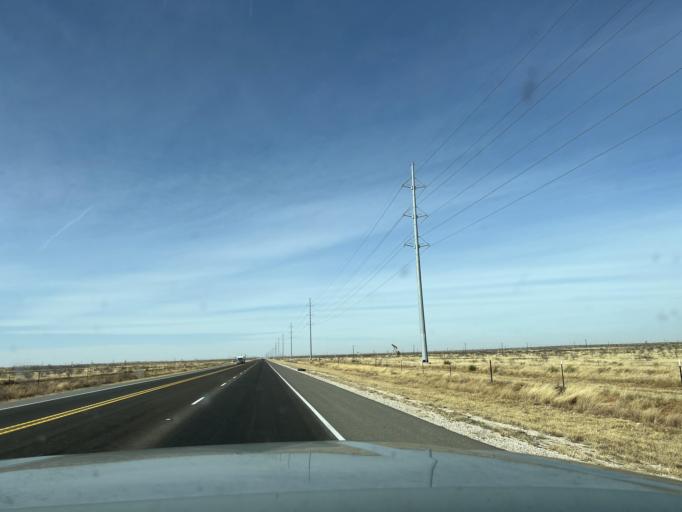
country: US
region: Texas
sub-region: Andrews County
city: Andrews
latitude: 32.3427
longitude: -102.6988
